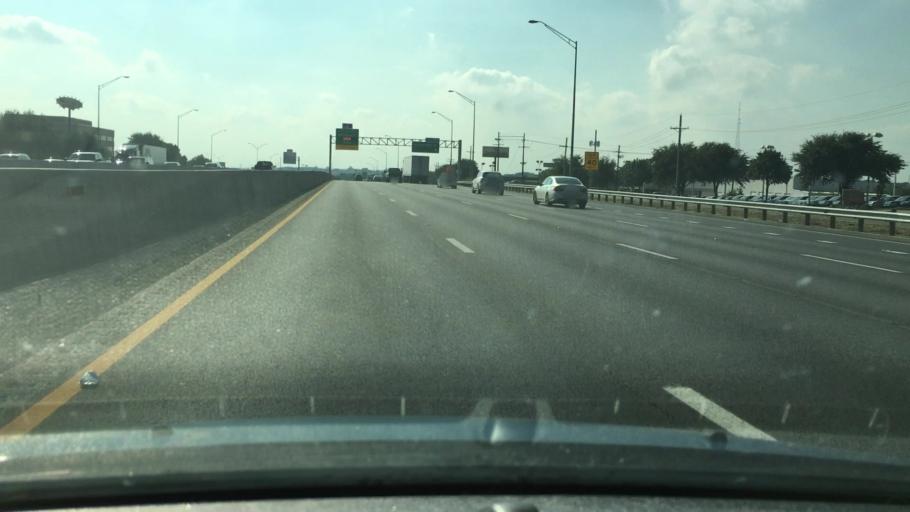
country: US
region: Texas
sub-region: Denton County
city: Lewisville
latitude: 33.0219
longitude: -96.9861
